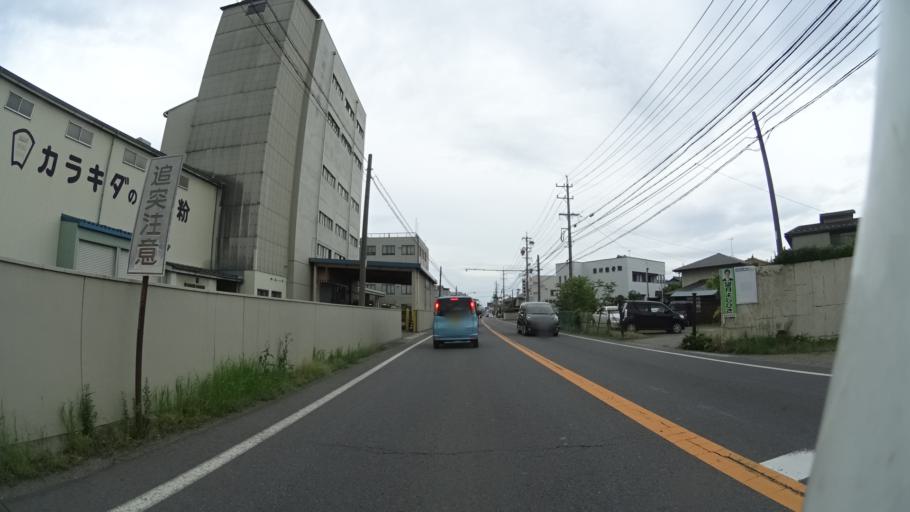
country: JP
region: Nagano
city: Nagano-shi
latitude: 36.5750
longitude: 138.1438
